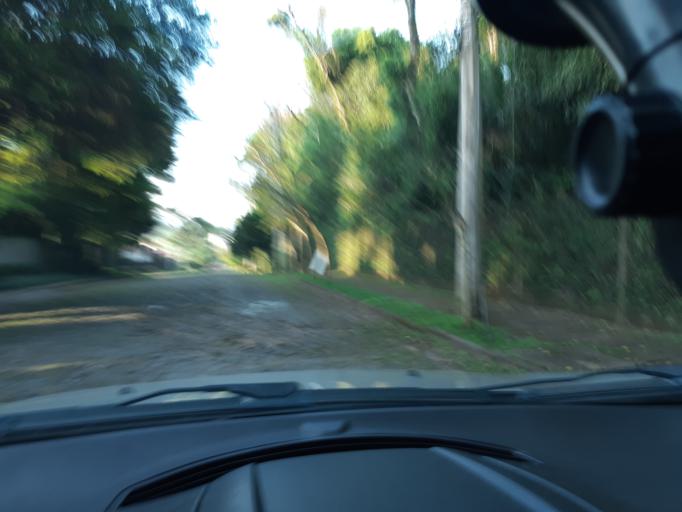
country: BR
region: Rio Grande do Sul
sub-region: Sao Leopoldo
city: Sao Leopoldo
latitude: -29.7766
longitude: -51.1402
